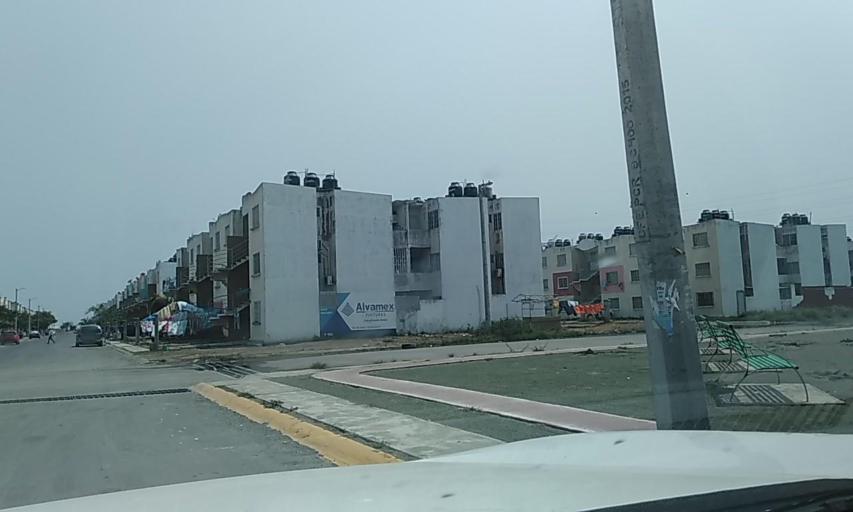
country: MX
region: Veracruz
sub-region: Veracruz
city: Las Amapolas
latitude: 19.1760
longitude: -96.1807
